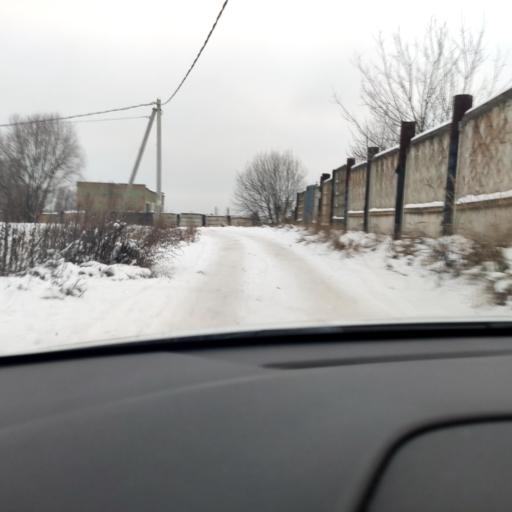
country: RU
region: Tatarstan
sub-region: Gorod Kazan'
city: Kazan
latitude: 55.8681
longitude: 49.1432
